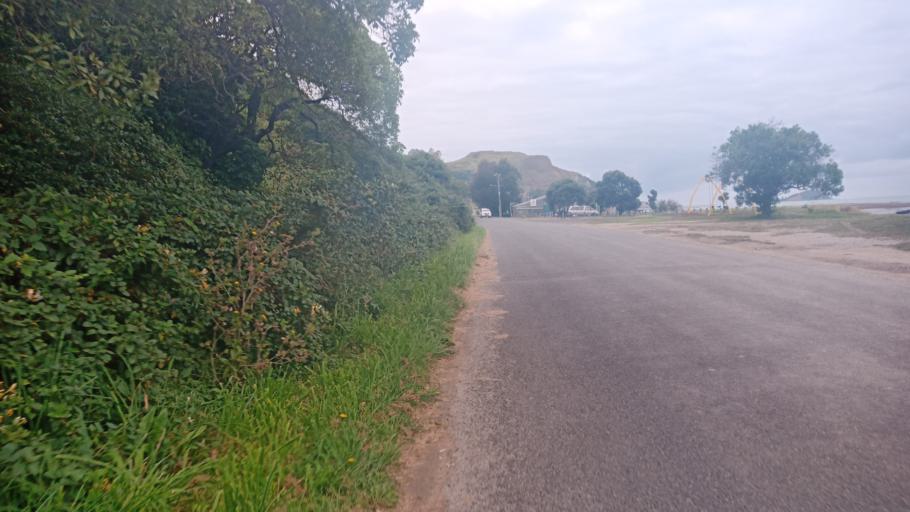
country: NZ
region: Gisborne
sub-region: Gisborne District
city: Gisborne
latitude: -38.6812
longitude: 178.0290
